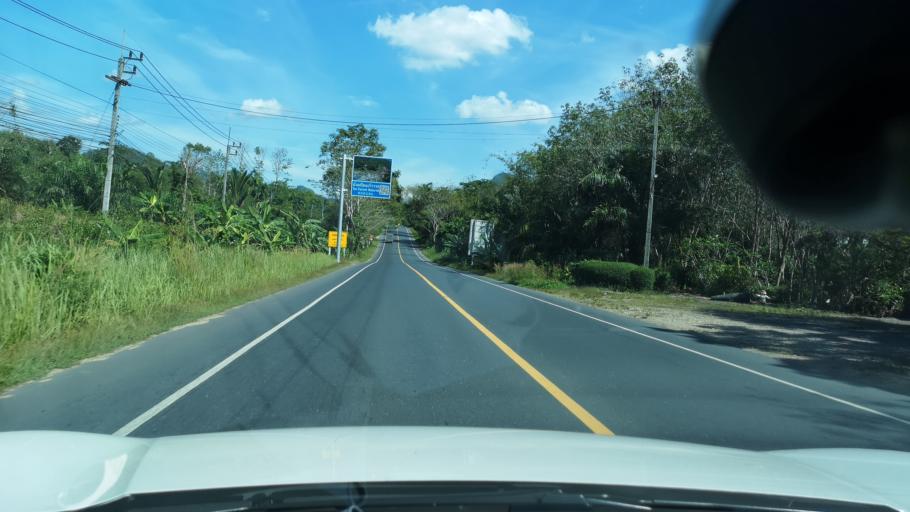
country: TH
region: Phangnga
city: Phang Nga
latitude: 8.5331
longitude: 98.5103
